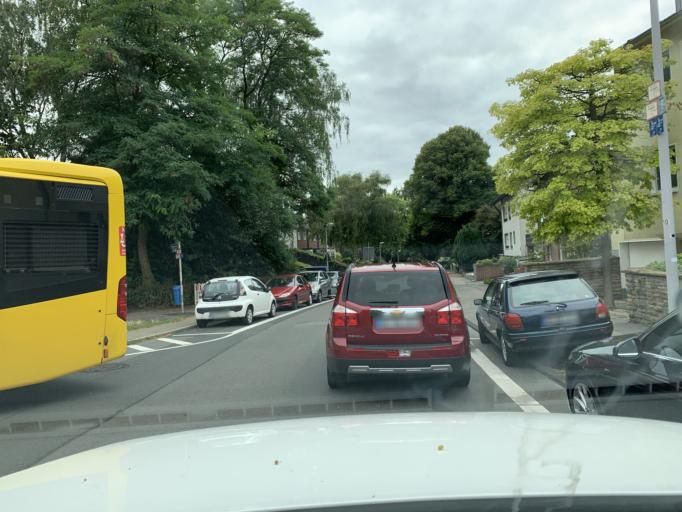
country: DE
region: North Rhine-Westphalia
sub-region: Regierungsbezirk Dusseldorf
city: Muelheim (Ruhr)
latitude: 51.4468
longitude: 6.9044
